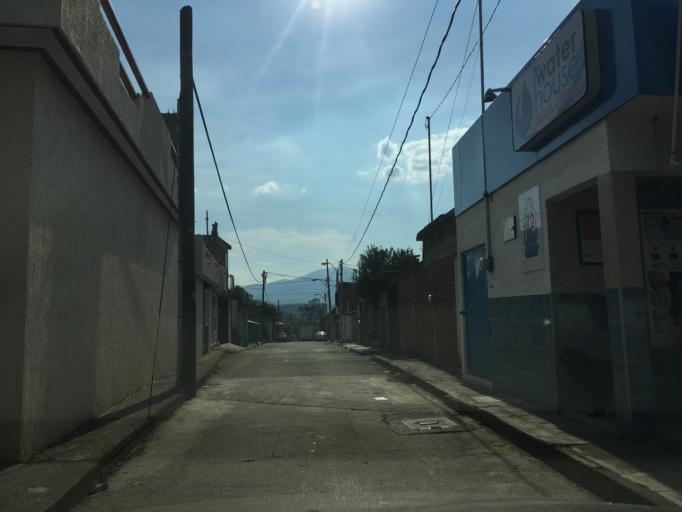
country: MX
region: Michoacan
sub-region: Morelia
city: Morelos
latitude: 19.6438
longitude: -101.2357
